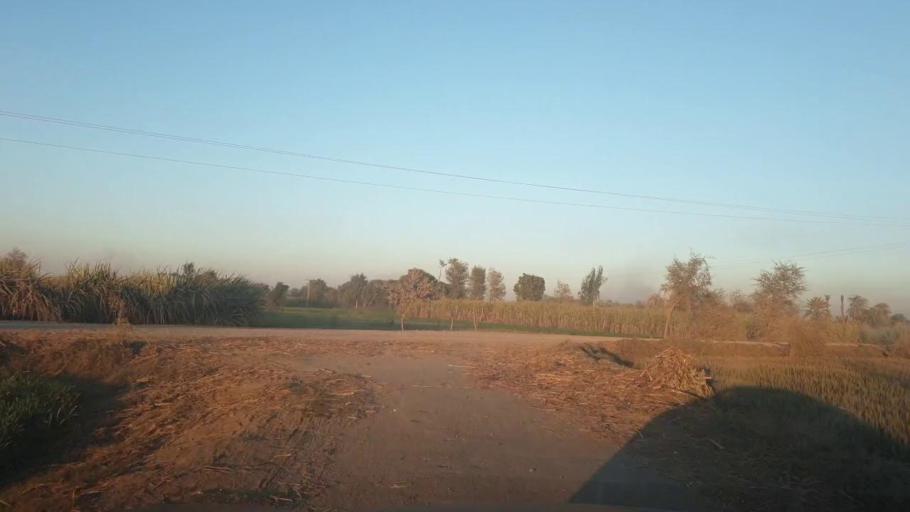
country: PK
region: Sindh
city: Ghotki
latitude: 28.0284
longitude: 69.2923
